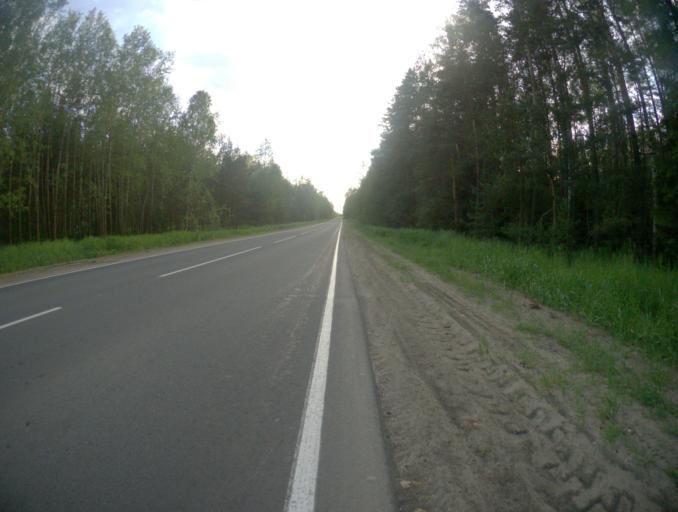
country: RU
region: Vladimir
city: Anopino
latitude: 55.6359
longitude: 40.7701
